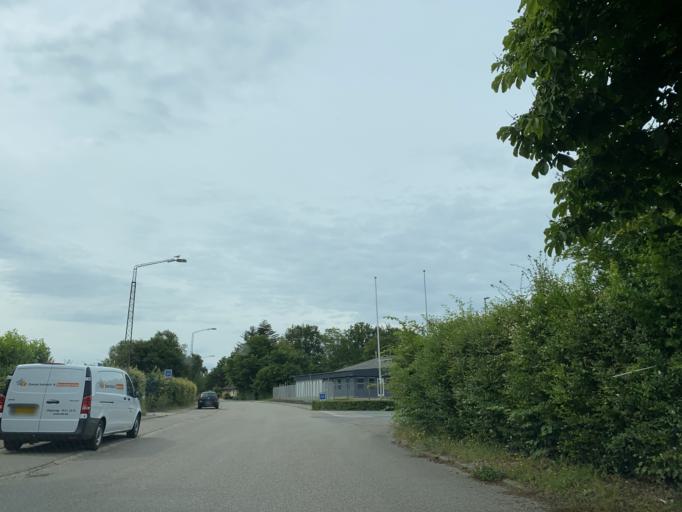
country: DK
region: South Denmark
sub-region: Sonderborg Kommune
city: Sonderborg
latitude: 54.9198
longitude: 9.8240
